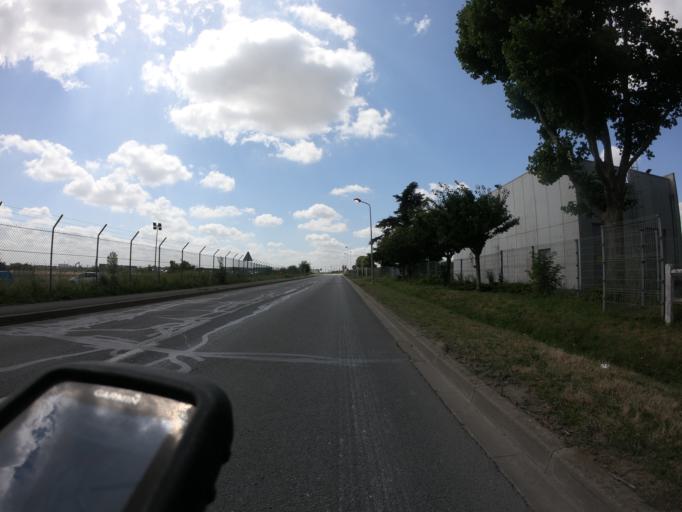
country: FR
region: Ile-de-France
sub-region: Departement du Val-de-Marne
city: Rungis
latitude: 48.7422
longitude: 2.3649
